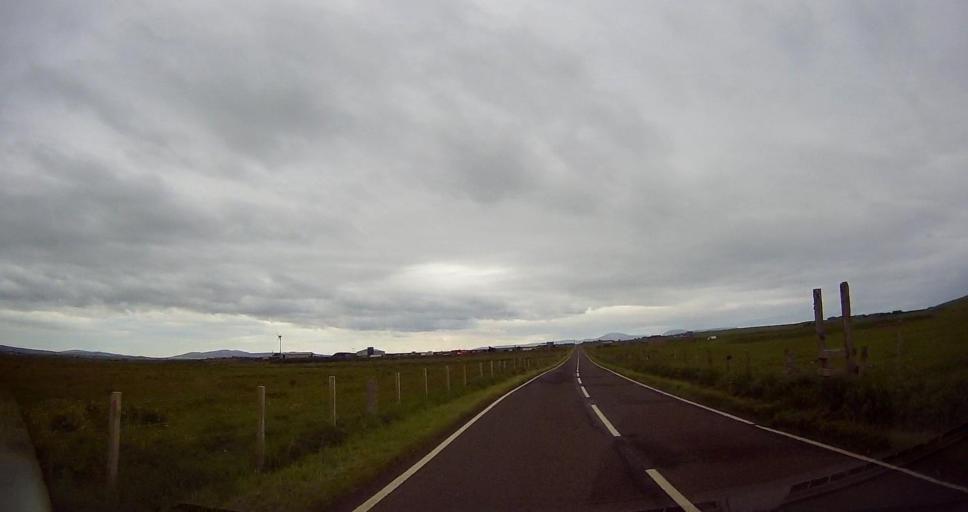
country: GB
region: Scotland
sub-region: Orkney Islands
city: Stromness
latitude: 59.0892
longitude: -3.2755
